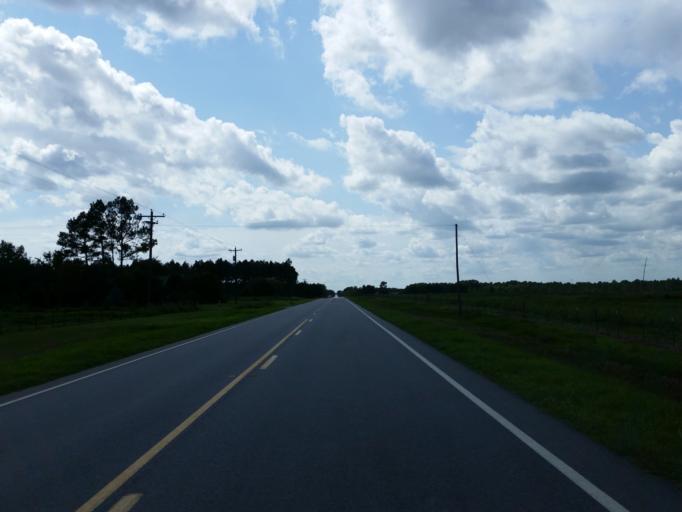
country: US
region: Georgia
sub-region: Turner County
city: Ashburn
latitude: 31.6416
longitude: -83.5278
